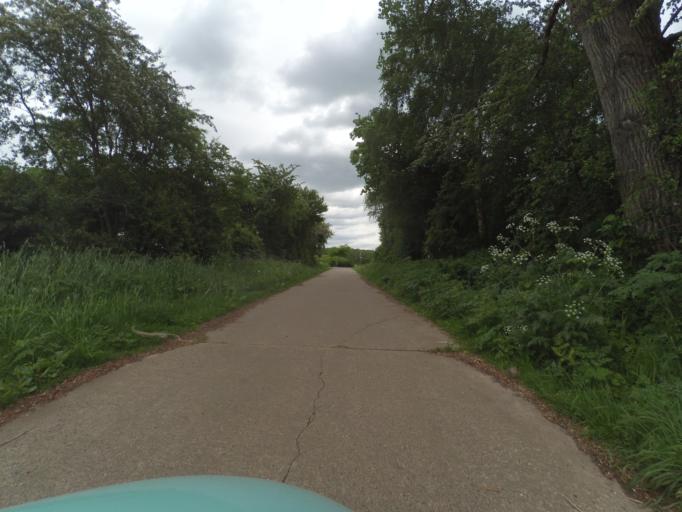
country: DE
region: Lower Saxony
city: Gross Munzel
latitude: 52.4234
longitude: 9.4977
